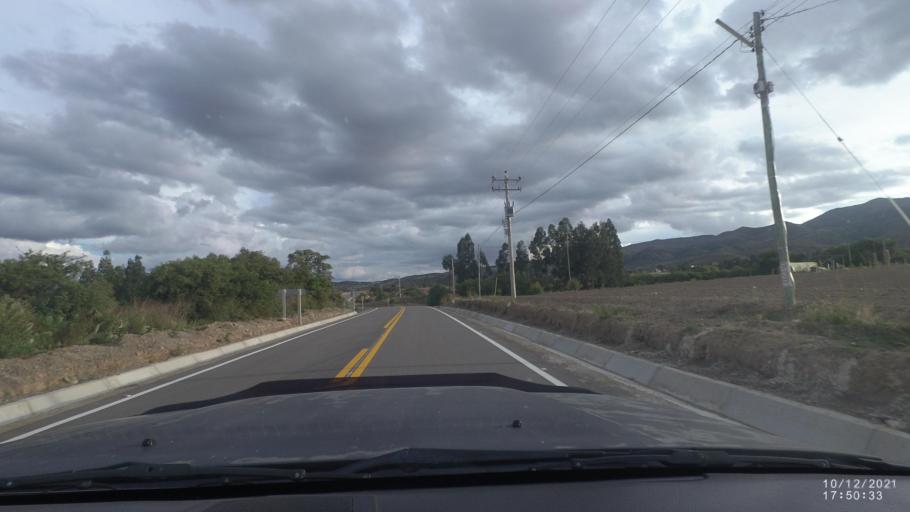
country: BO
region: Cochabamba
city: Tarata
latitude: -17.6675
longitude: -65.9633
